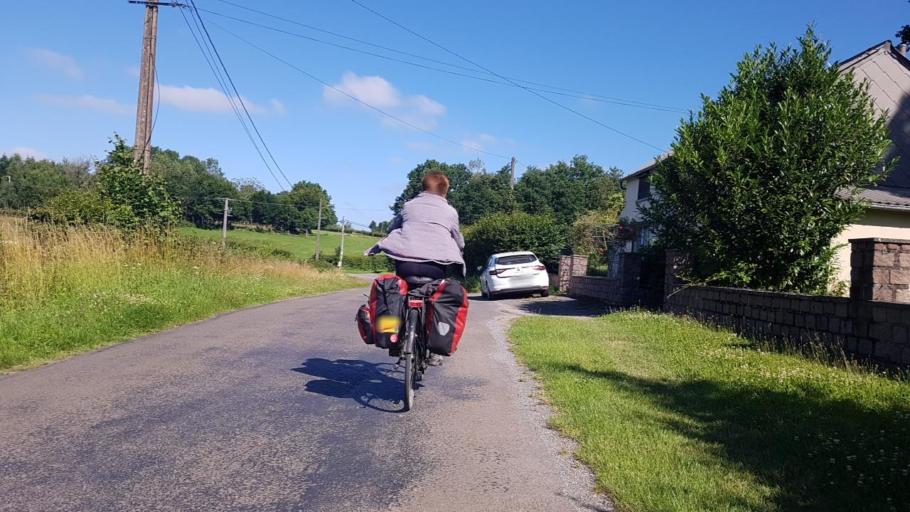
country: FR
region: Nord-Pas-de-Calais
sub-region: Departement du Nord
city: Anor
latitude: 49.9840
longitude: 4.1266
